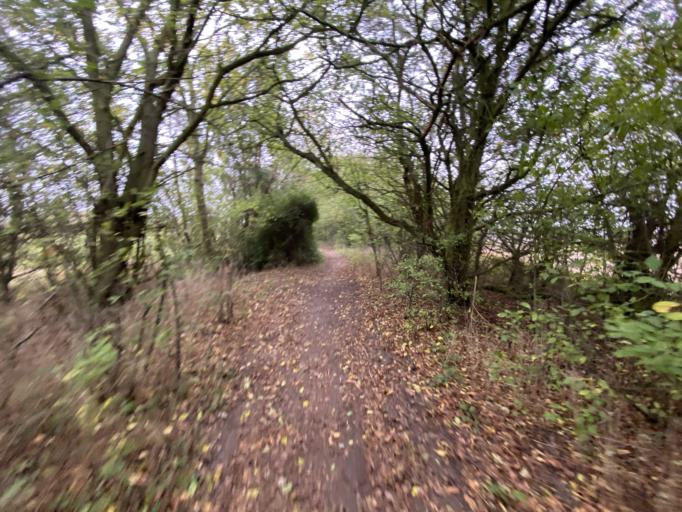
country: DK
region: Capital Region
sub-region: Dragor Kommune
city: Dragor
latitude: 55.5982
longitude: 12.6519
